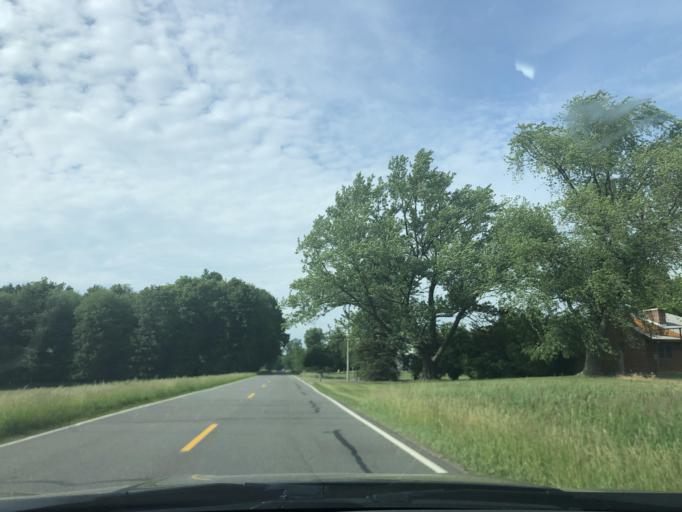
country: US
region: Michigan
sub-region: Clinton County
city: Bath
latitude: 42.8394
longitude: -84.4838
